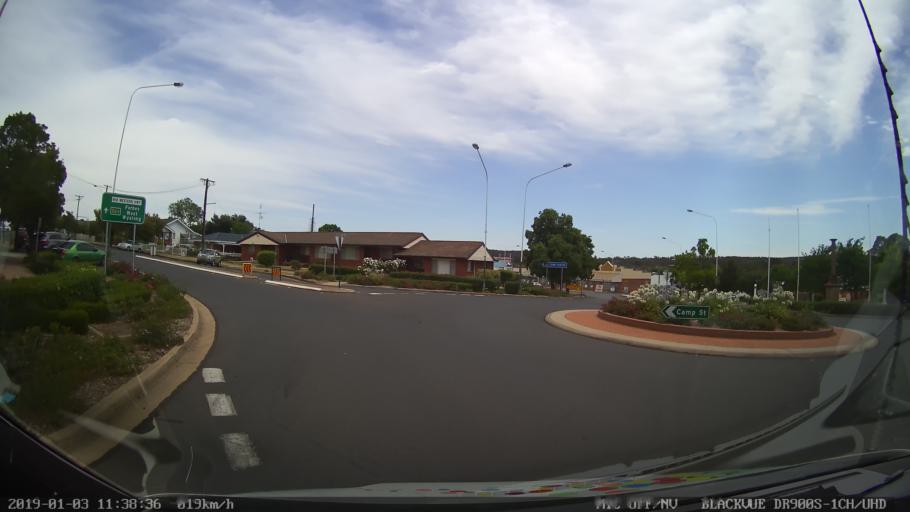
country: AU
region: New South Wales
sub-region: Weddin
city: Grenfell
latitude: -33.8953
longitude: 148.1626
